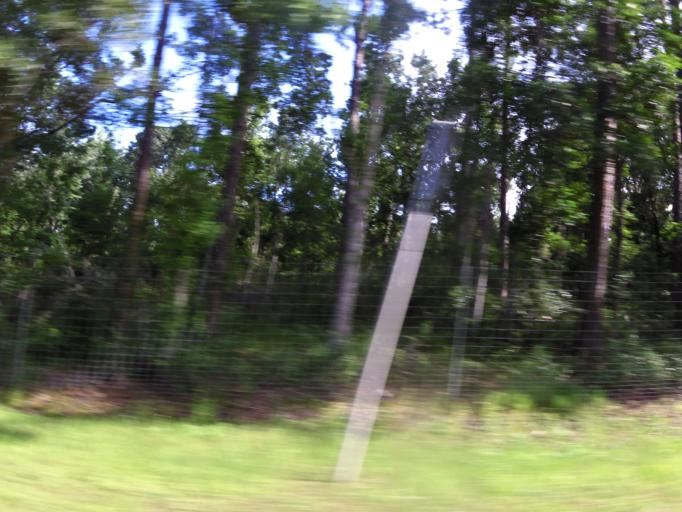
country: US
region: Florida
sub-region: Clay County
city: Green Cove Springs
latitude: 30.0149
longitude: -81.5671
